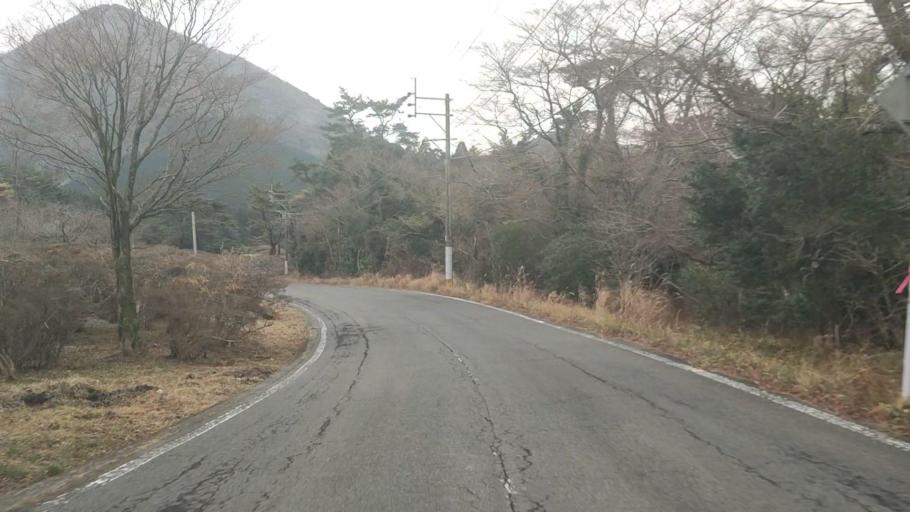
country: JP
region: Nagasaki
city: Shimabara
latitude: 32.7485
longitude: 130.2743
